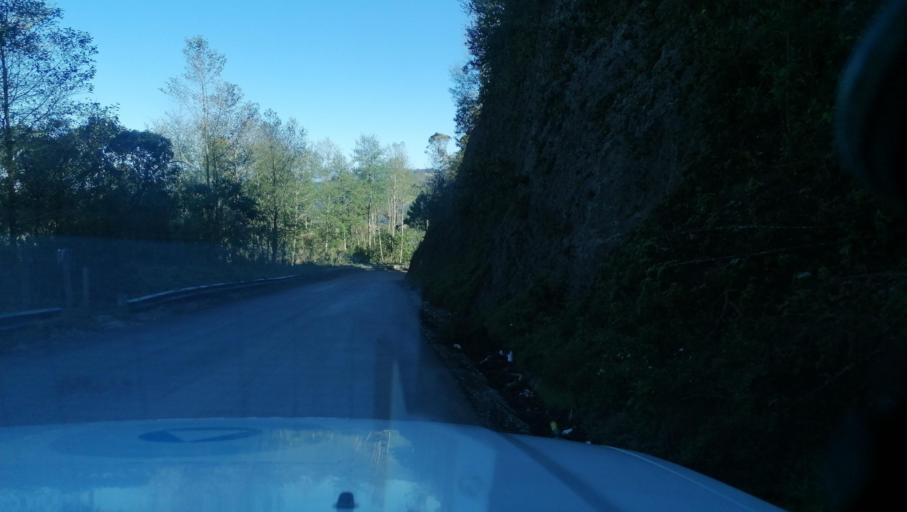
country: MX
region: Chiapas
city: Motozintla de Mendoza
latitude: 15.2739
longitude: -92.2332
